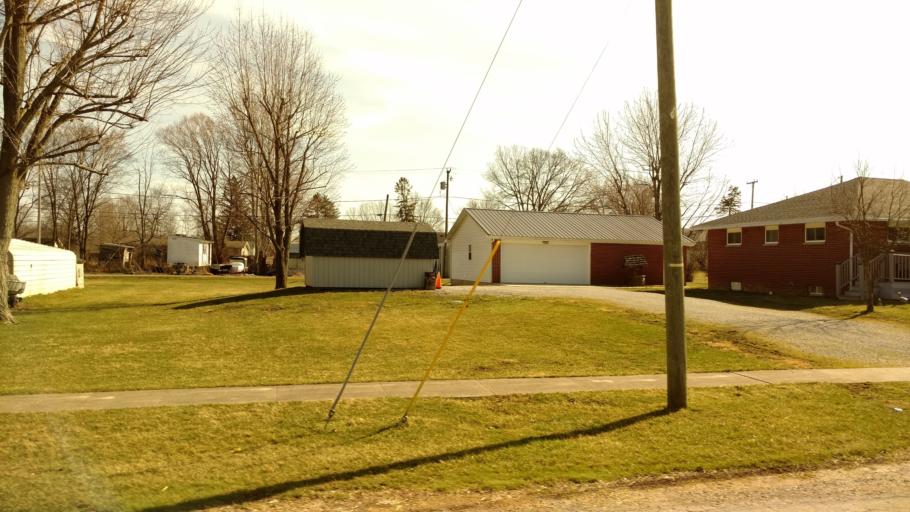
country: US
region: Ohio
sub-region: Hardin County
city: Forest
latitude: 40.7023
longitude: -83.3908
